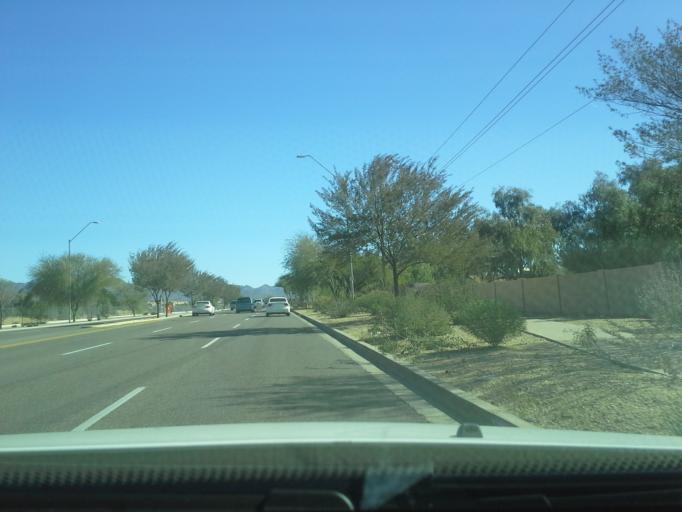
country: US
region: Arizona
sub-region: Maricopa County
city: Paradise Valley
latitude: 33.6393
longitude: -111.9313
